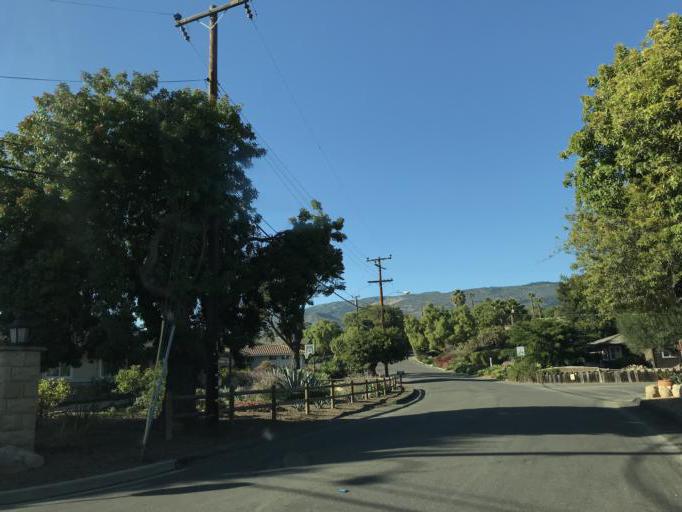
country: US
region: California
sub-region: Santa Barbara County
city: Goleta
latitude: 34.4589
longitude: -119.8201
